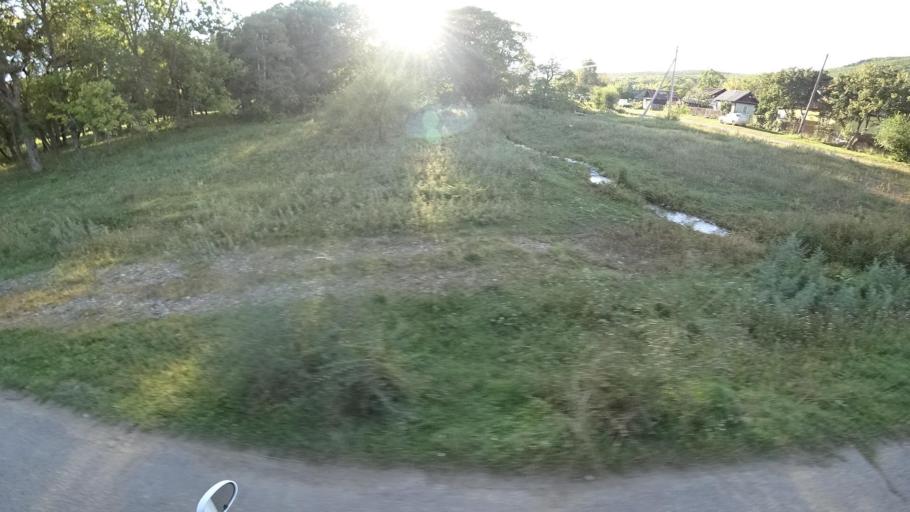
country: RU
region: Primorskiy
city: Kirovskiy
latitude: 44.8290
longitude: 133.5751
